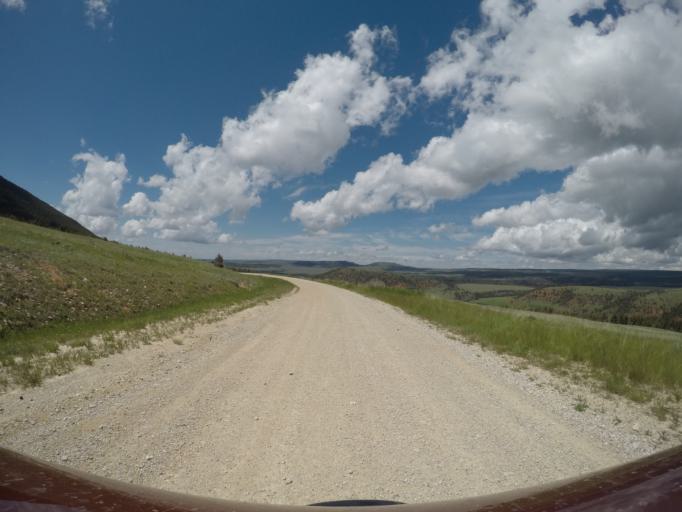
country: US
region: Wyoming
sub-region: Big Horn County
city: Lovell
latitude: 45.1907
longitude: -108.4761
